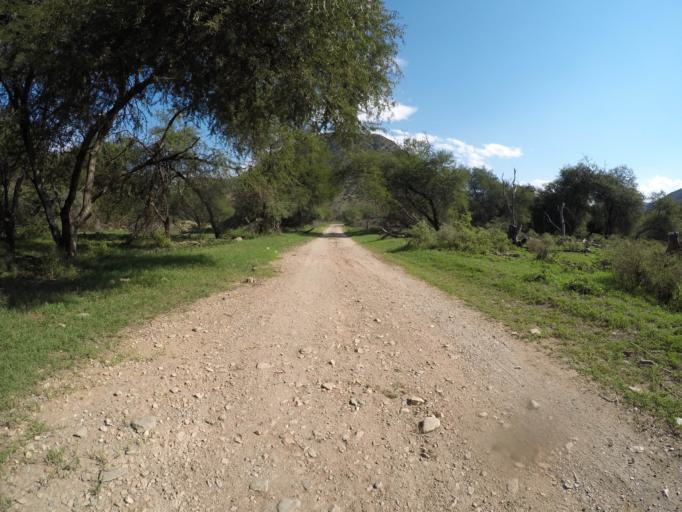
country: ZA
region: Eastern Cape
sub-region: Cacadu District Municipality
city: Kareedouw
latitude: -33.6672
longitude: 24.3832
